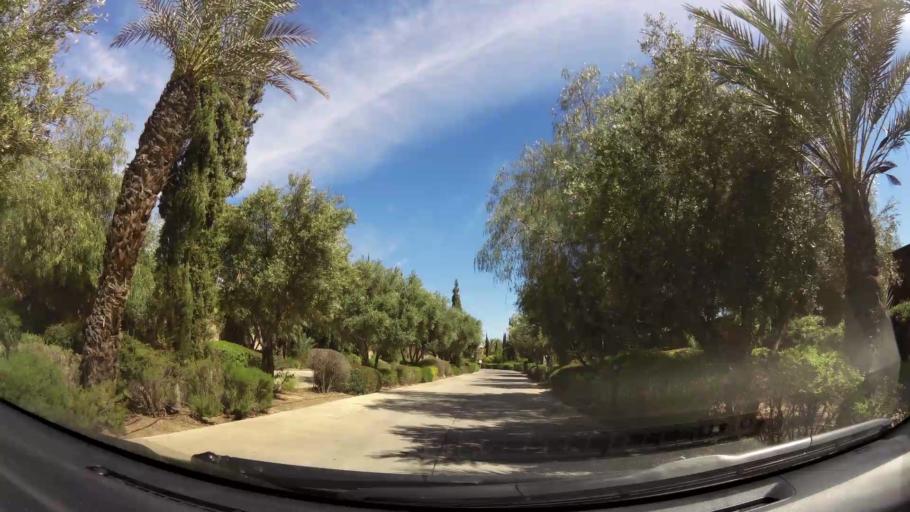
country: MA
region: Marrakech-Tensift-Al Haouz
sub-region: Marrakech
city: Marrakesh
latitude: 31.6015
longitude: -7.9515
